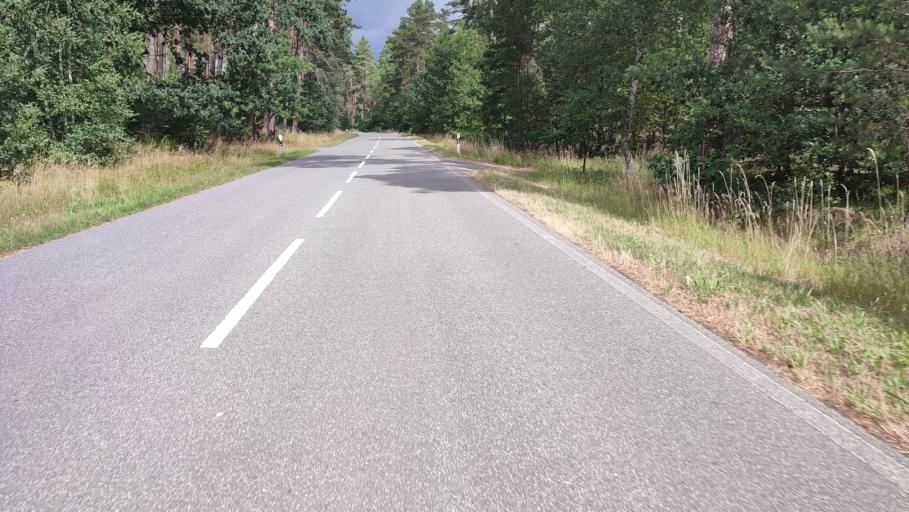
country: DE
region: Lower Saxony
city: Hitzacker
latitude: 53.1899
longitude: 11.1054
